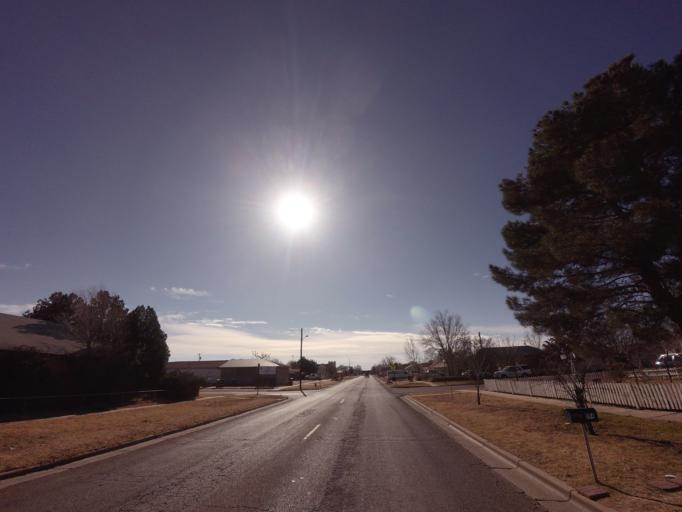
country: US
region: New Mexico
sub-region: Curry County
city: Clovis
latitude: 34.4032
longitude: -103.2142
